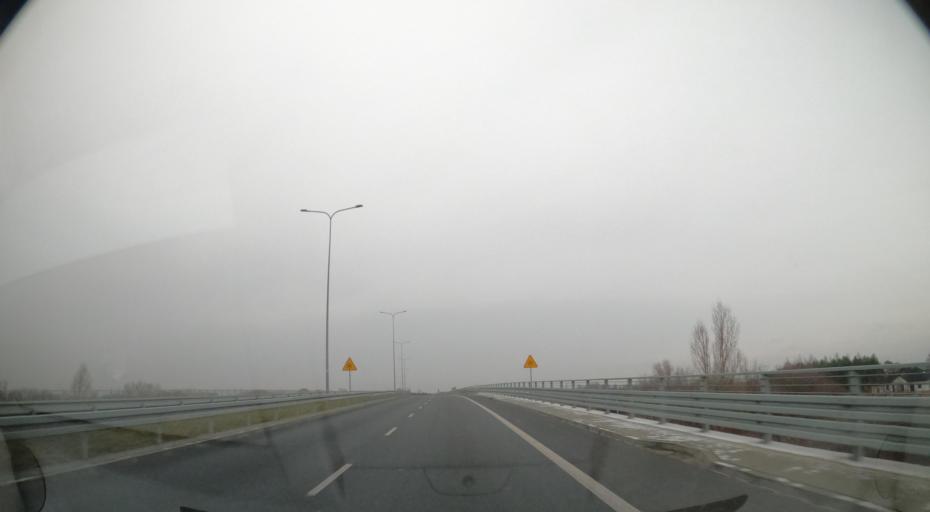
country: PL
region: Masovian Voivodeship
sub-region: Radom
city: Radom
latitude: 51.4073
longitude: 21.2028
